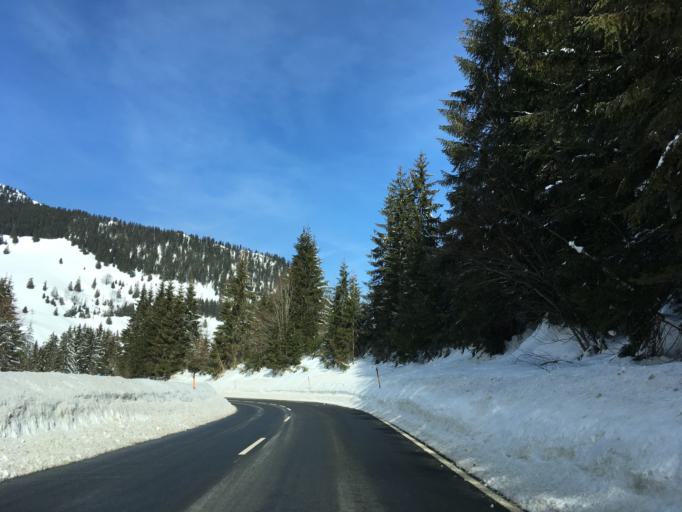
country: DE
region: Bavaria
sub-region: Upper Bavaria
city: Bayrischzell
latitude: 47.6855
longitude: 12.0575
